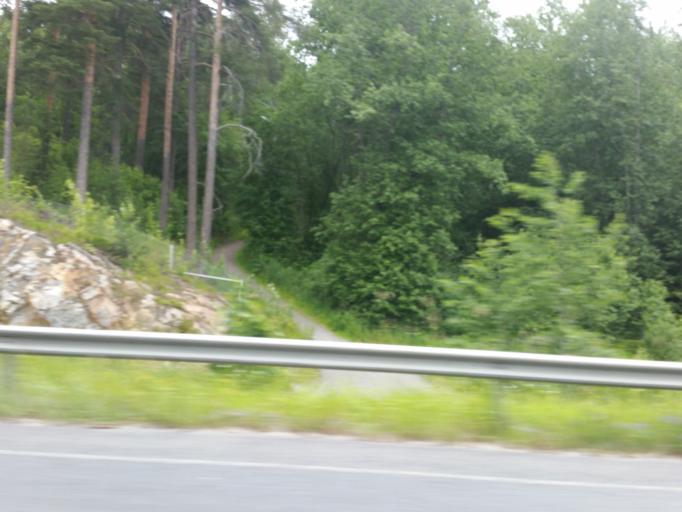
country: FI
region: Northern Savo
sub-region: Kuopio
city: Kuopio
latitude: 62.8828
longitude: 27.6481
